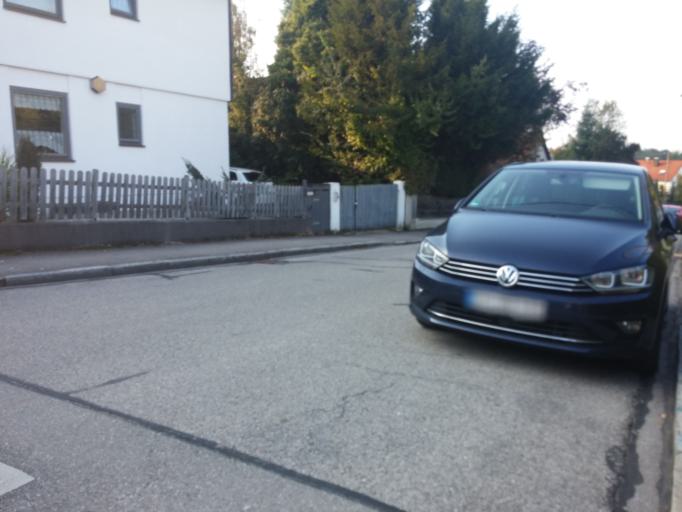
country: DE
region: Bavaria
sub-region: Upper Bavaria
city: Zorneding
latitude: 48.0874
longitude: 11.8326
